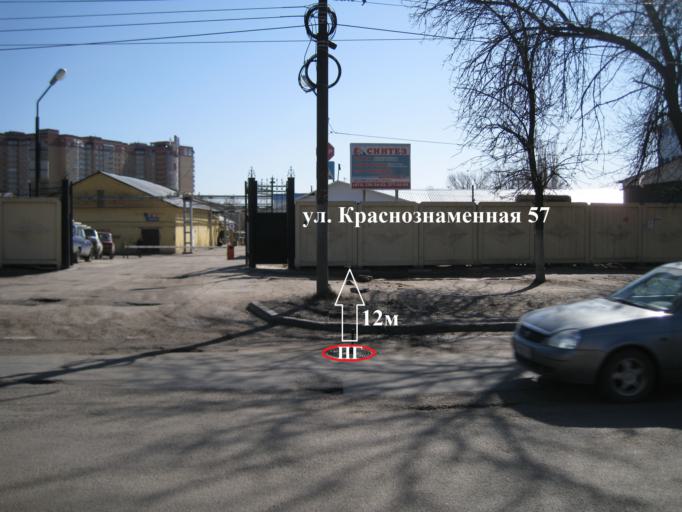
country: RU
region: Voronezj
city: Voronezh
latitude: 51.6474
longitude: 39.1846
